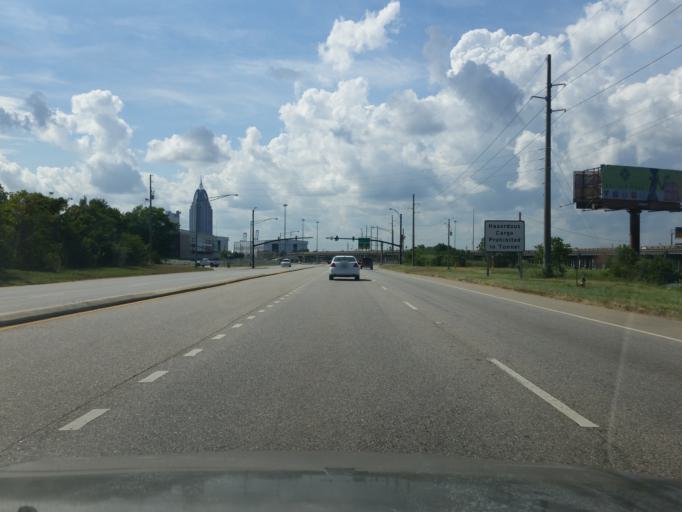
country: US
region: Alabama
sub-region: Mobile County
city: Mobile
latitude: 30.6892
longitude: -88.0205
